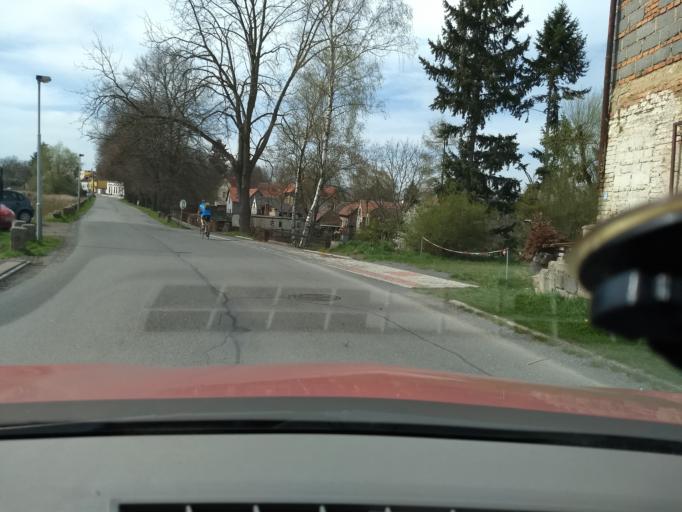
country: CZ
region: Central Bohemia
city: Hostivice
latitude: 50.0698
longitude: 14.2455
